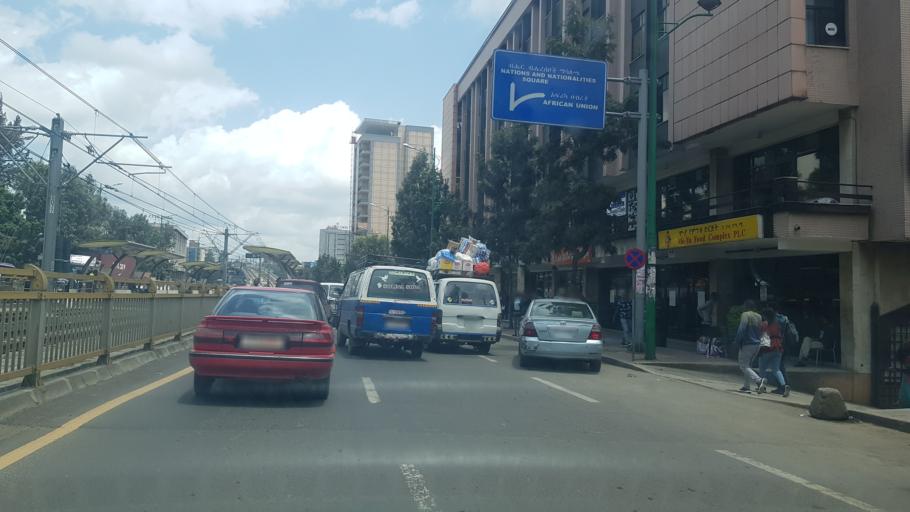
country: ET
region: Adis Abeba
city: Addis Ababa
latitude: 8.9910
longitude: 38.7590
